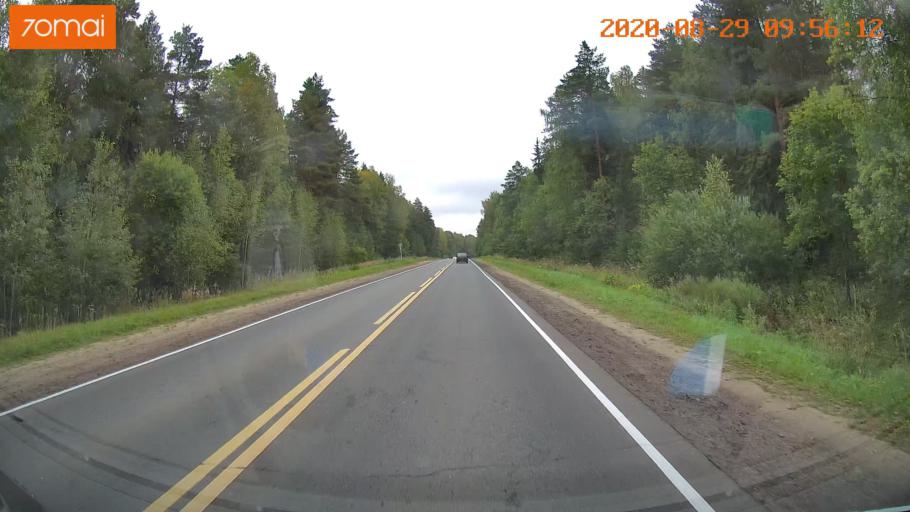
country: RU
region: Ivanovo
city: Zarechnyy
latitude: 57.4211
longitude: 42.2832
